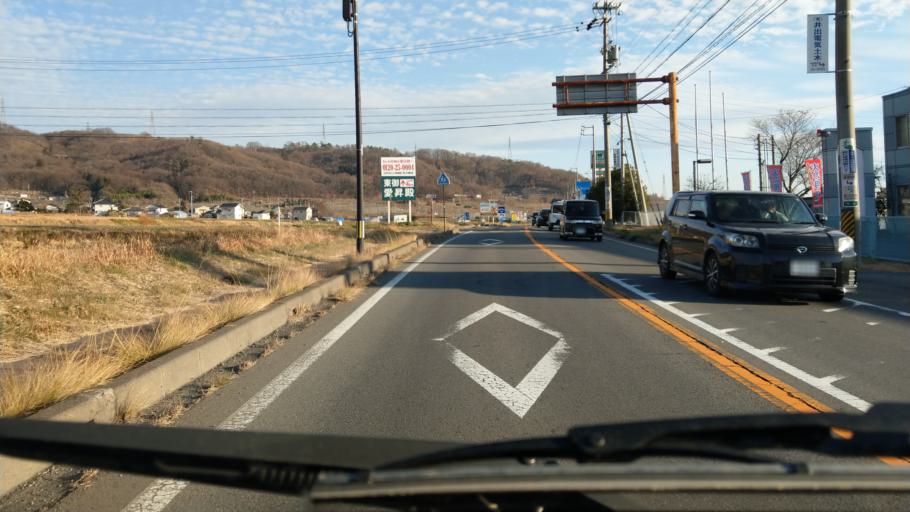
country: JP
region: Nagano
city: Ueda
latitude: 36.3924
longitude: 138.3023
